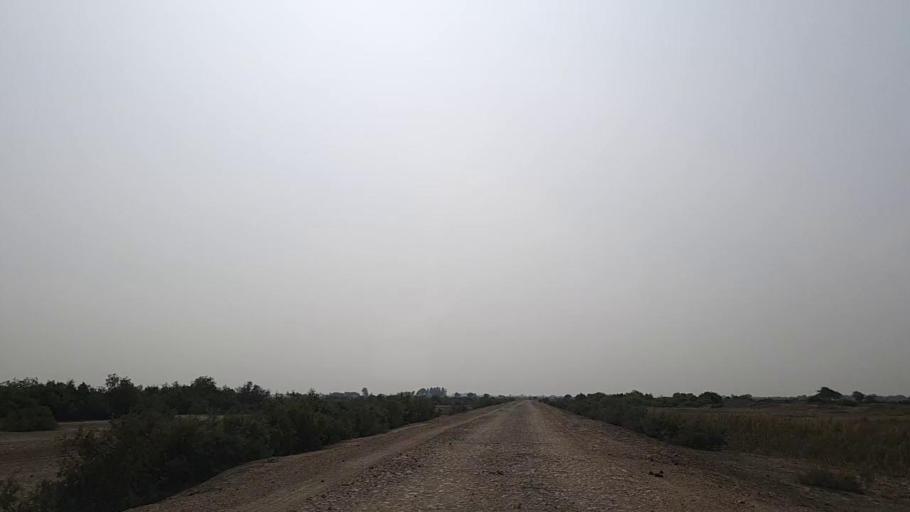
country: PK
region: Sindh
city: Mirpur Sakro
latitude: 24.6428
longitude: 67.7676
